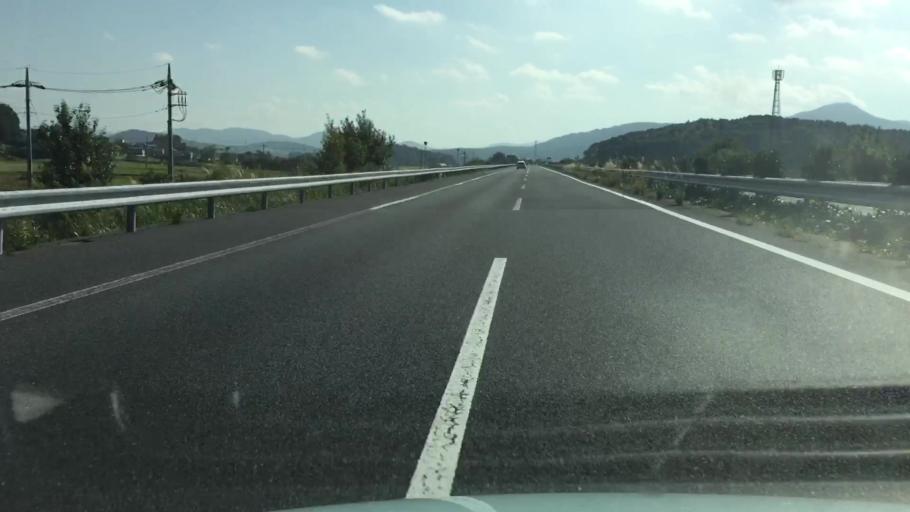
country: JP
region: Ibaraki
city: Iwase
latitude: 36.3643
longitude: 140.0679
